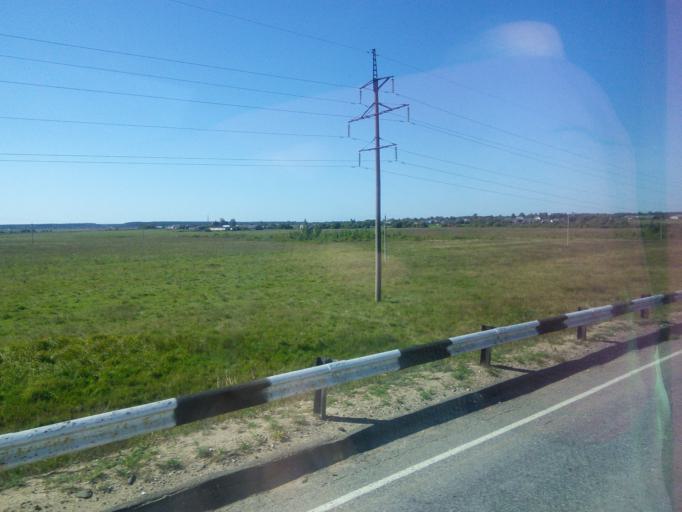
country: RU
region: Tverskaya
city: Kalyazin
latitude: 57.2336
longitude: 37.7869
